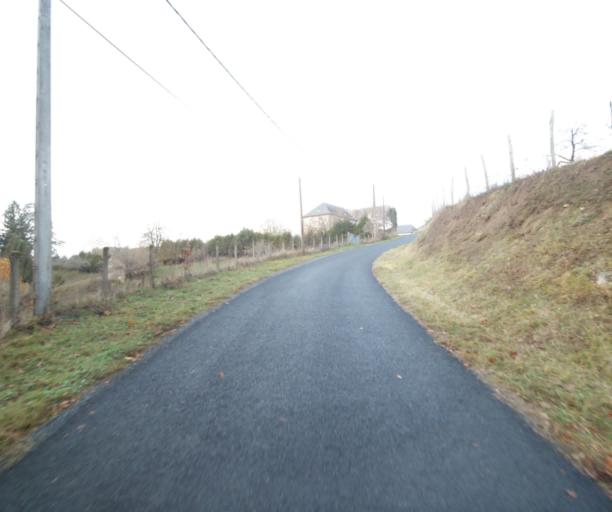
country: FR
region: Limousin
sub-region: Departement de la Correze
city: Cornil
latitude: 45.2049
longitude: 1.6907
